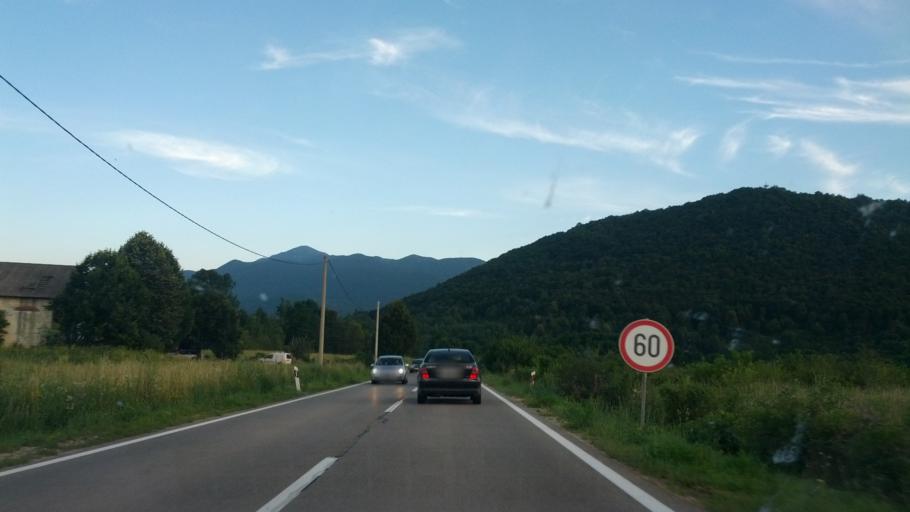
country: BA
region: Federation of Bosnia and Herzegovina
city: Izacic
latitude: 44.8954
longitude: 15.7243
